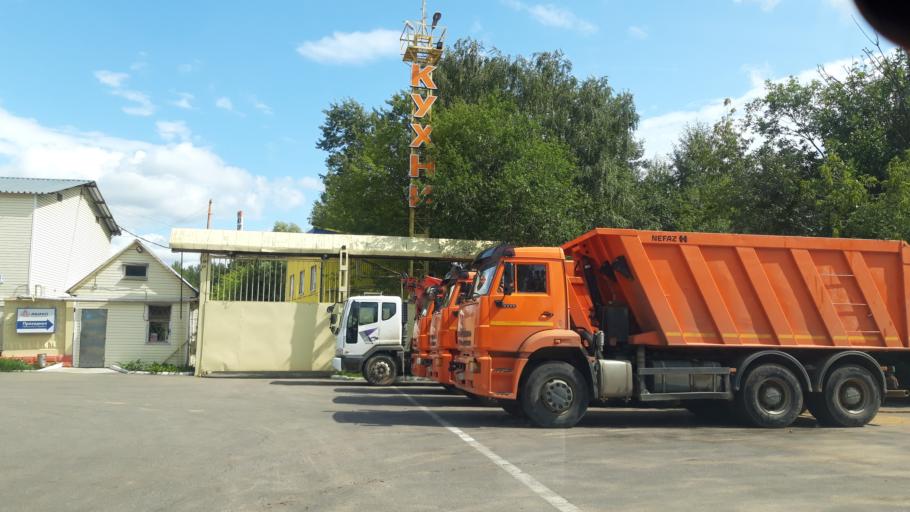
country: RU
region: Moscow
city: Zelenograd
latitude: 55.9690
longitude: 37.1906
